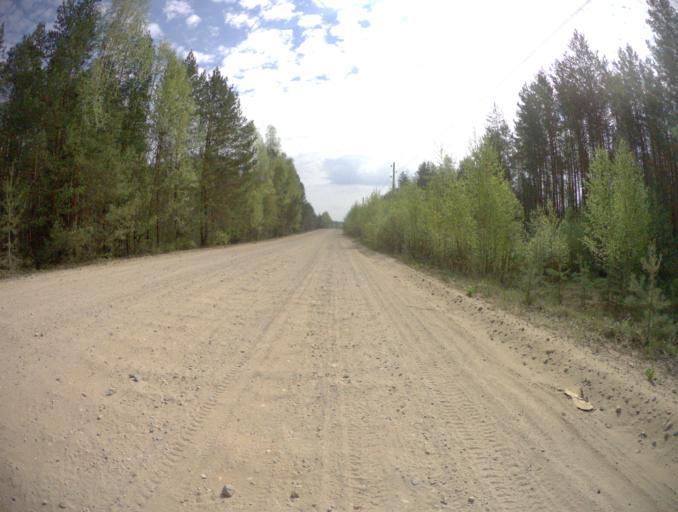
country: RU
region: Ivanovo
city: Yuzha
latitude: 56.5197
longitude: 42.0844
